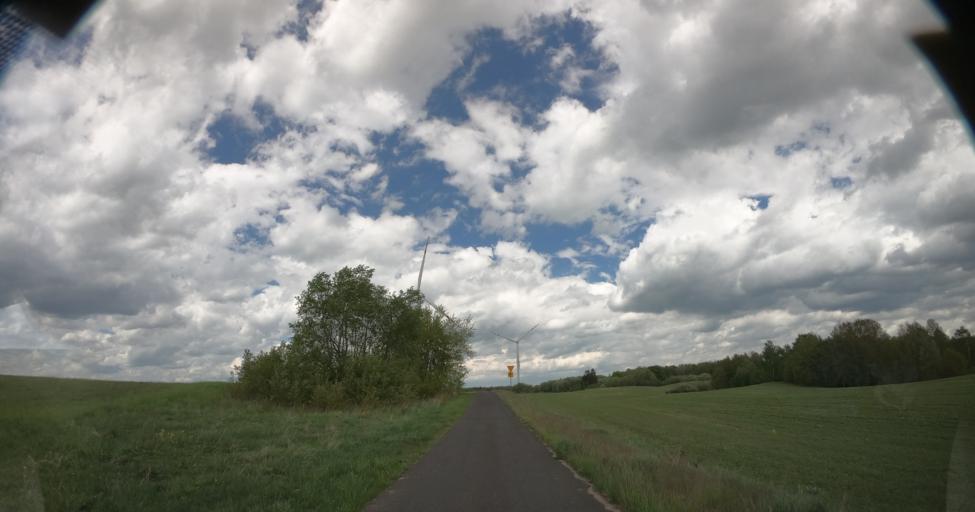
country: PL
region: West Pomeranian Voivodeship
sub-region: Powiat drawski
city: Drawsko Pomorskie
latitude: 53.5540
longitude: 15.7810
